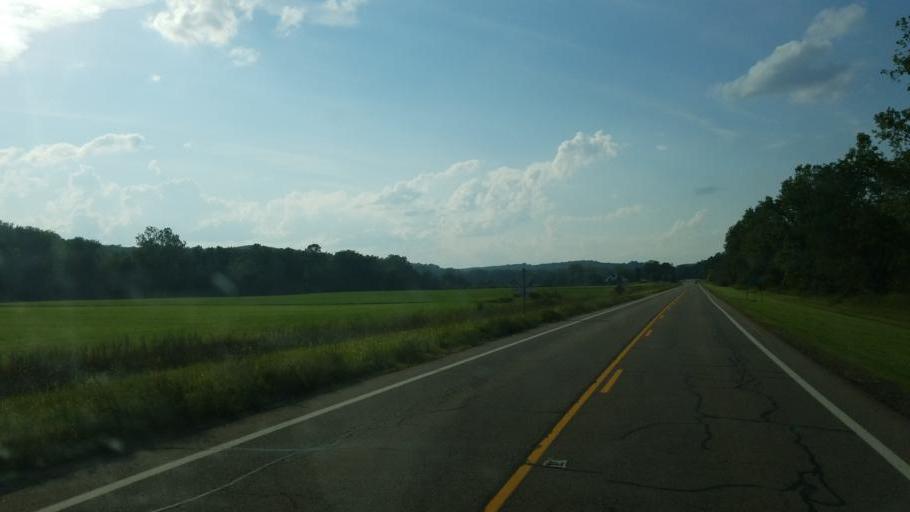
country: US
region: Ohio
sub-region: Knox County
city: Gambier
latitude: 40.3633
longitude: -82.3889
